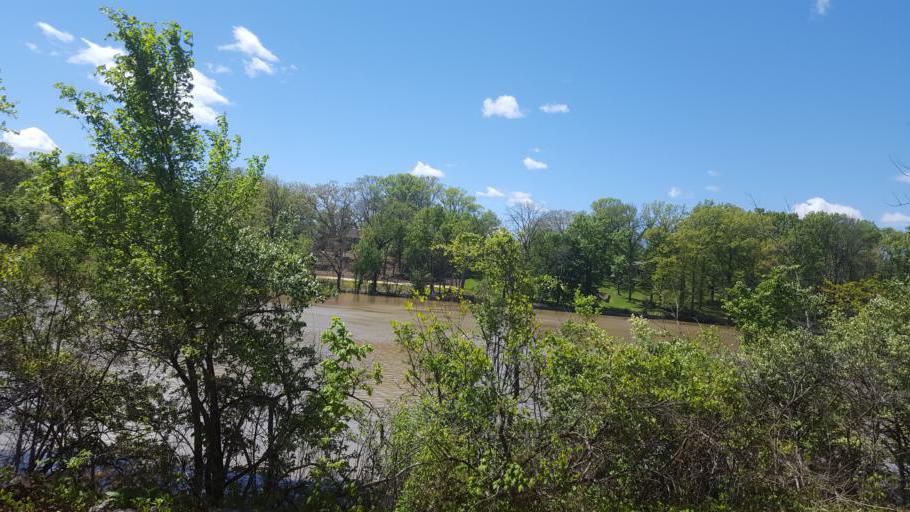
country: US
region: Ohio
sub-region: Franklin County
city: Dublin
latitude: 40.0458
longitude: -83.0954
